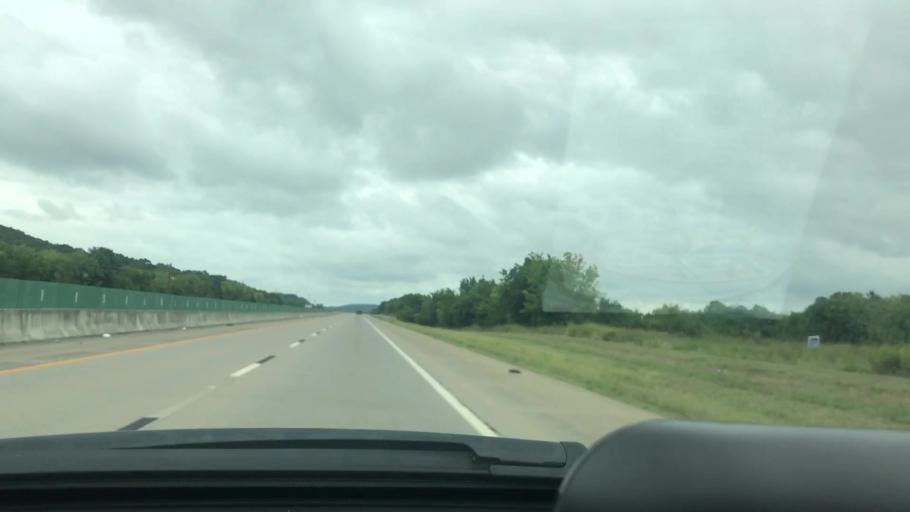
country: US
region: Oklahoma
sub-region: Pittsburg County
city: Krebs
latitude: 35.0703
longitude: -95.7048
